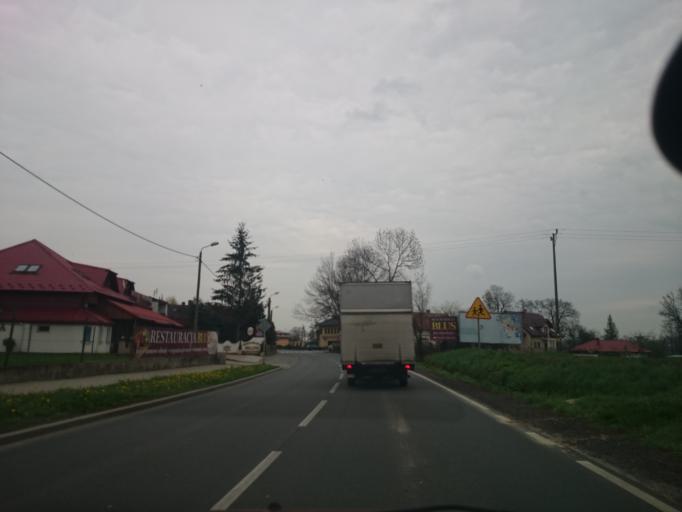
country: PL
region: Opole Voivodeship
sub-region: Powiat nyski
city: Otmuchow
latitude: 50.4449
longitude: 17.1132
